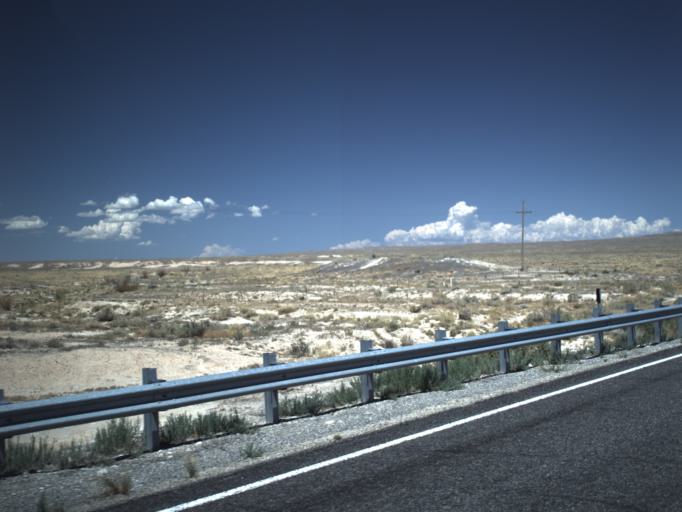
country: US
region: Utah
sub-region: Millard County
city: Delta
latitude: 39.1174
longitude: -113.1254
